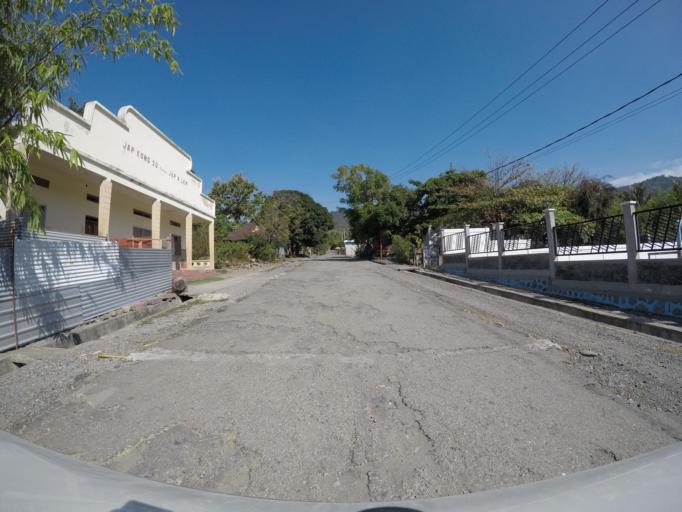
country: TL
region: Liquica
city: Maubara
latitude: -8.6139
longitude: 125.2066
